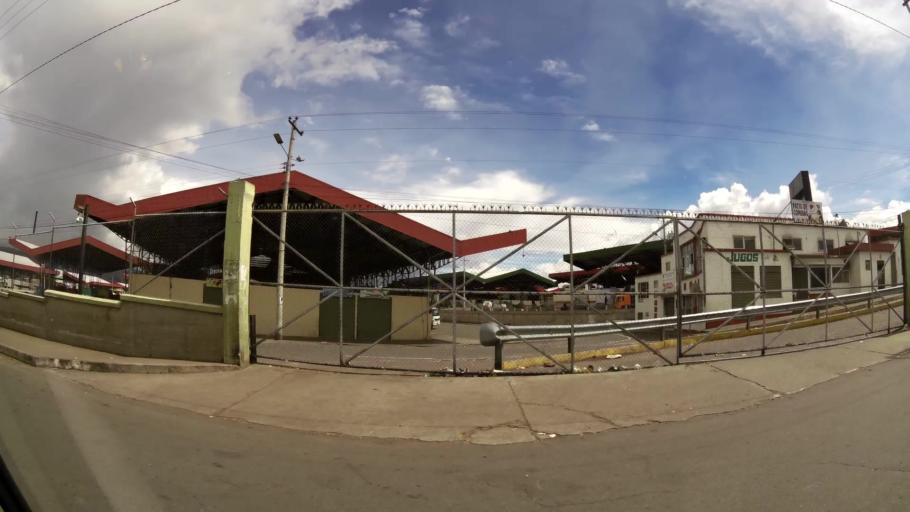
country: EC
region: Tungurahua
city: Ambato
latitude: -1.2692
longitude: -78.6152
